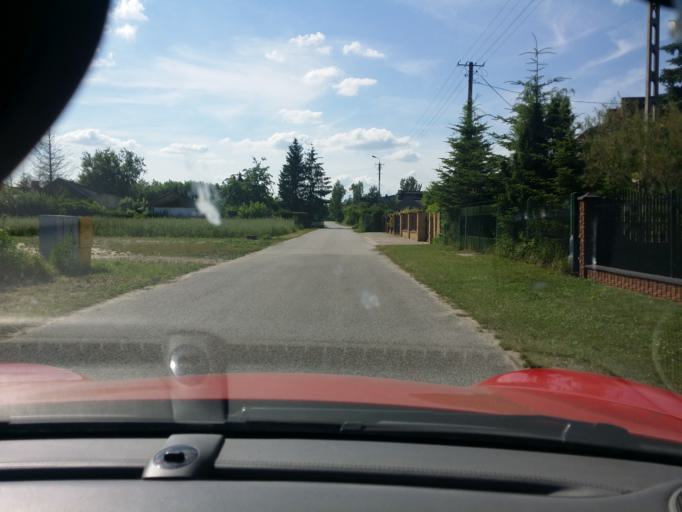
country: PL
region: Masovian Voivodeship
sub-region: Powiat radomski
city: Trablice
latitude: 51.3466
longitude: 21.1421
